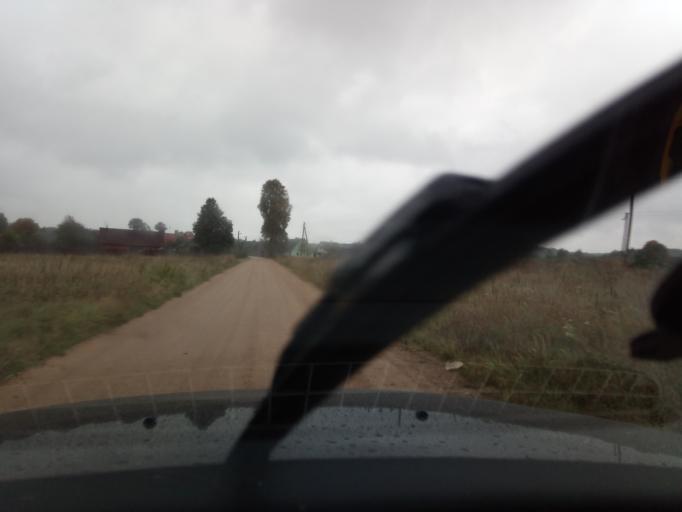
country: LT
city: Skaidiskes
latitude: 54.5963
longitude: 25.5795
